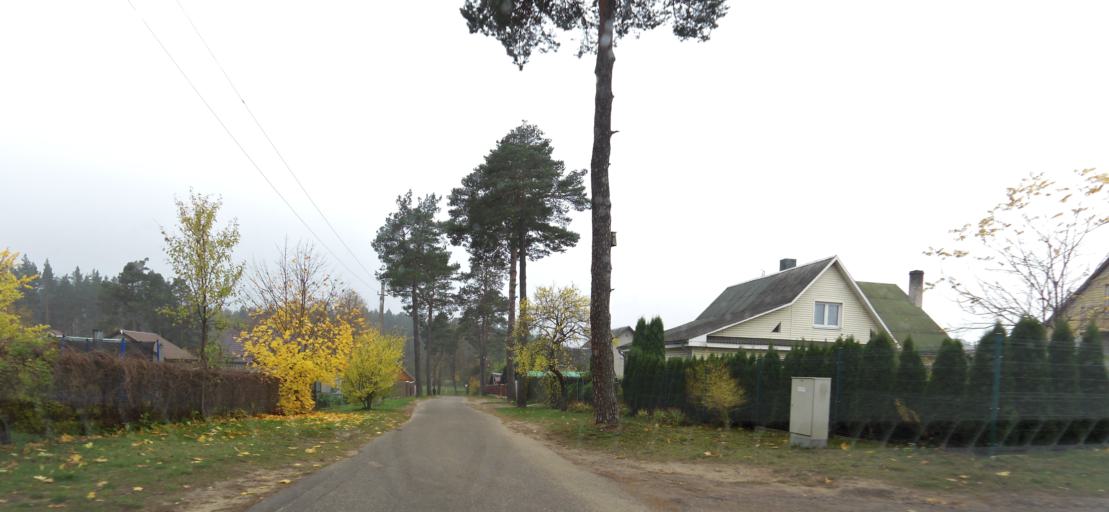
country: BY
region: Grodnenskaya
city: Astravyets
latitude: 54.6357
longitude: 25.6870
